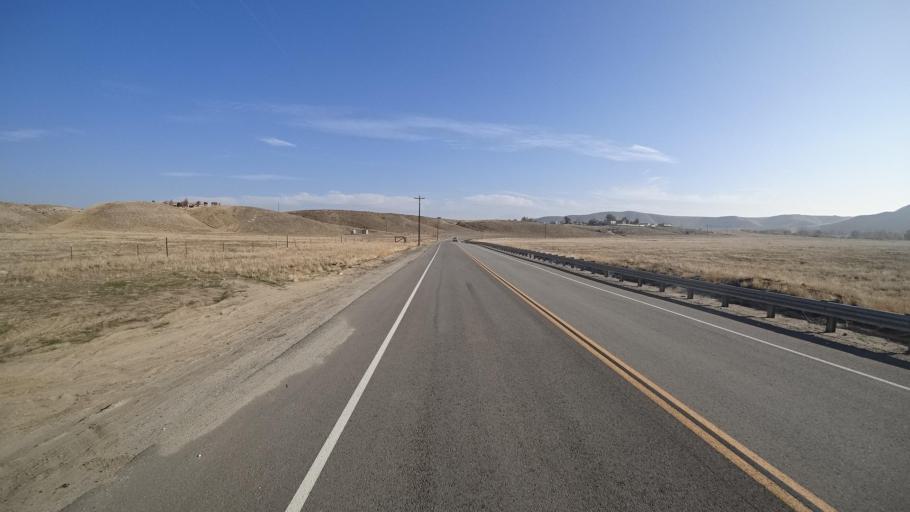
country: US
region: California
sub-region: Kern County
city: Oildale
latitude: 35.4456
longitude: -118.8975
